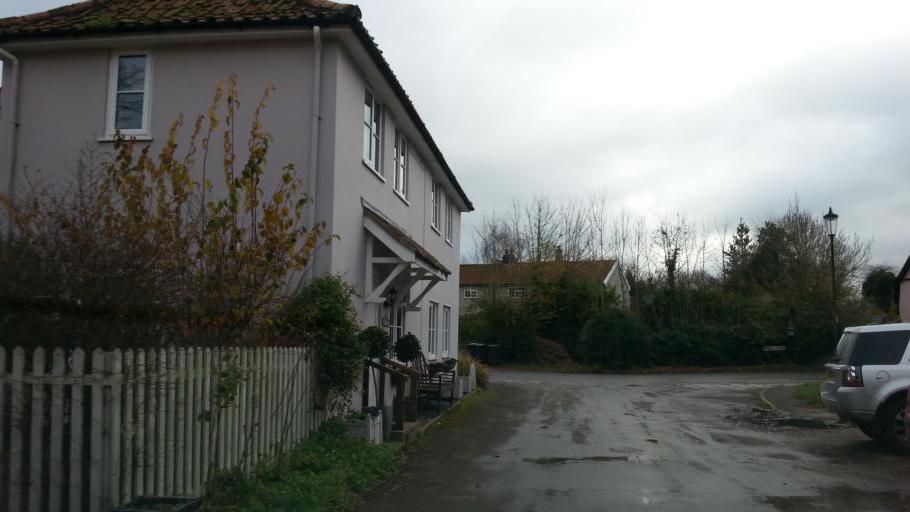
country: GB
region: England
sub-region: Suffolk
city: Cookley
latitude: 52.3024
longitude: 1.3675
